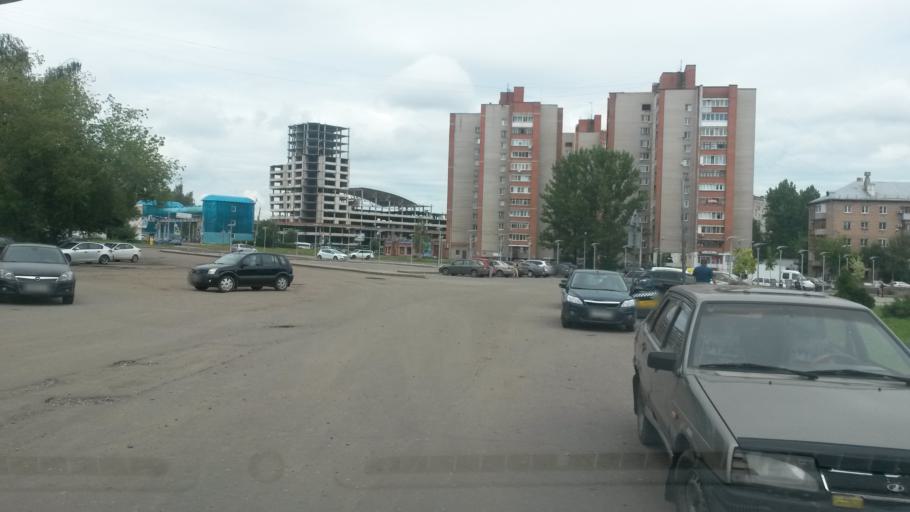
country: RU
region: Jaroslavl
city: Yaroslavl
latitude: 57.5911
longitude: 39.8656
